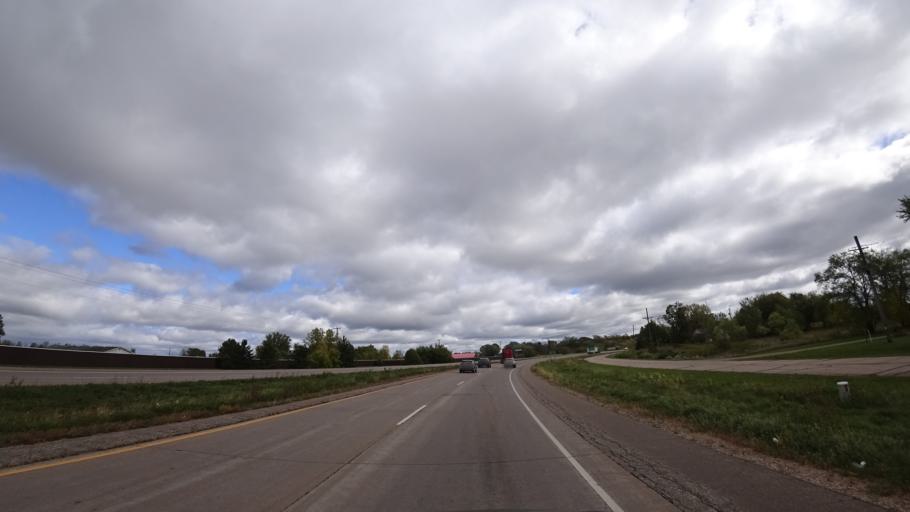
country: US
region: Wisconsin
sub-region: Eau Claire County
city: Eau Claire
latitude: 44.8435
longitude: -91.5607
